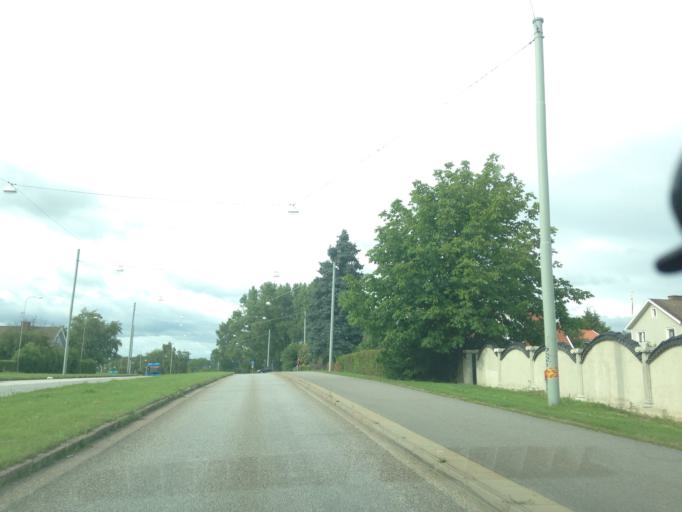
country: SE
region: Vaestra Goetaland
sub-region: Goteborg
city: Goeteborg
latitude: 57.7371
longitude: 11.9732
